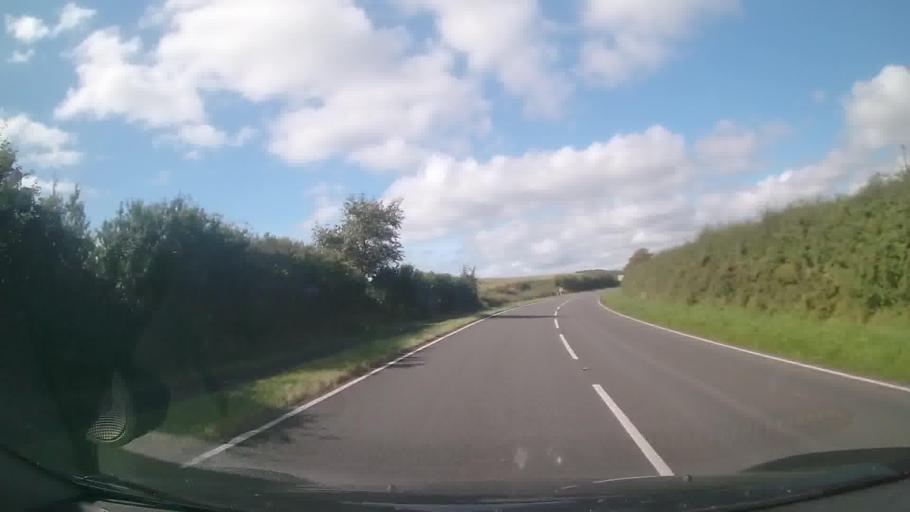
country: GB
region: Wales
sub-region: Pembrokeshire
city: Penally
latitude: 51.6572
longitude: -4.7252
